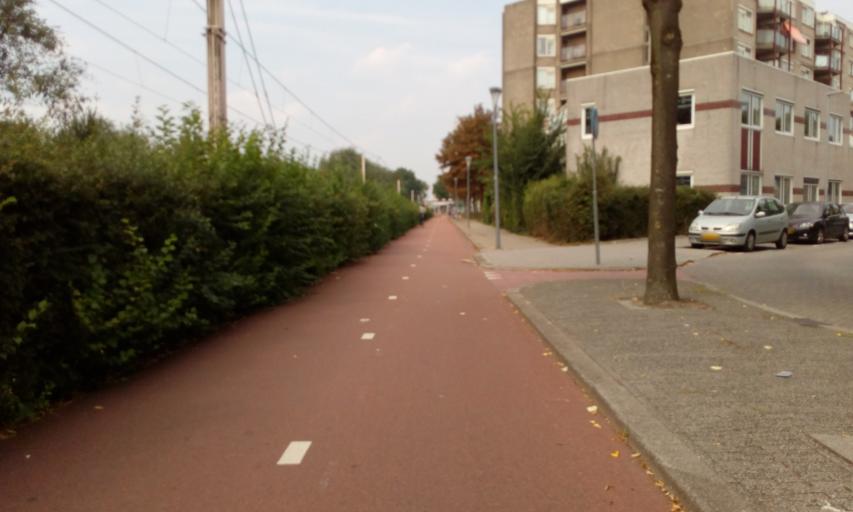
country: NL
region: South Holland
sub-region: Gemeente Rotterdam
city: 's-Gravenland
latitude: 51.9433
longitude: 4.5556
